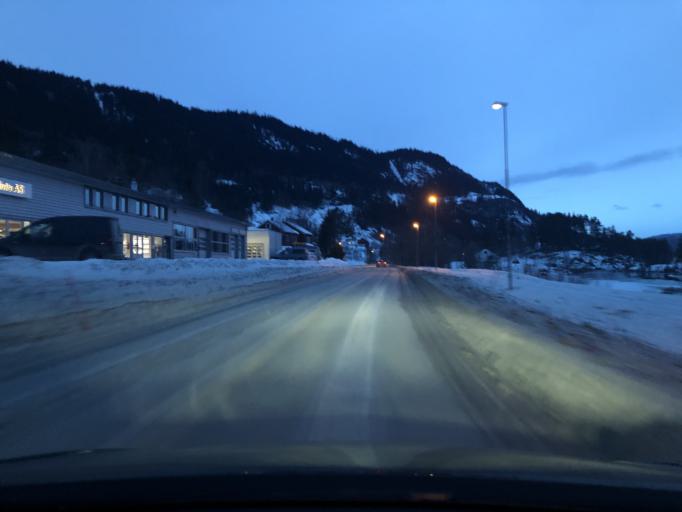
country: NO
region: Oppland
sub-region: Nord-Aurdal
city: Fagernes
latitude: 60.9905
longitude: 9.2220
